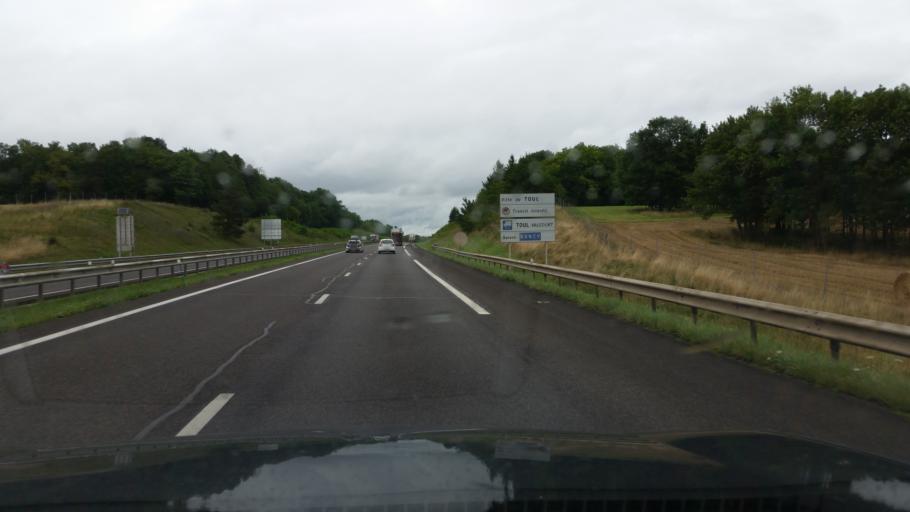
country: FR
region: Lorraine
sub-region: Departement de Meurthe-et-Moselle
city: Dommartin-les-Toul
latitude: 48.6354
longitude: 5.8814
